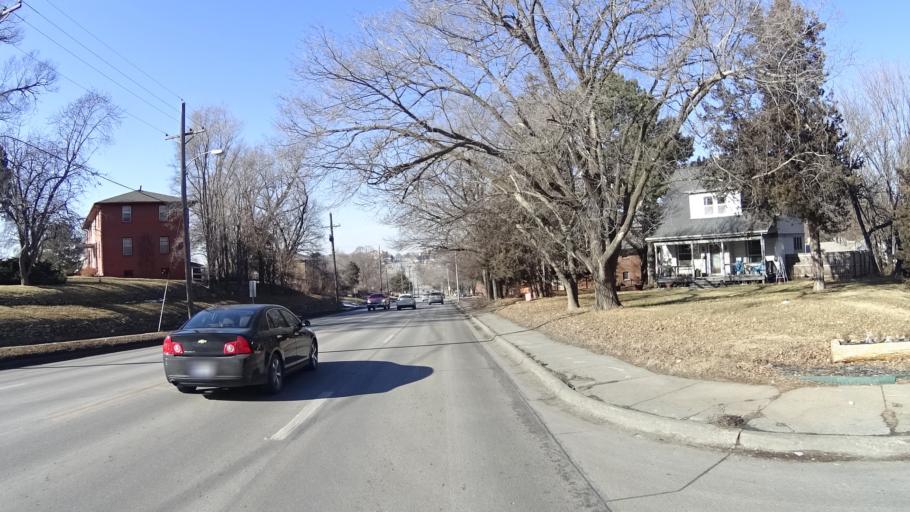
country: US
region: Nebraska
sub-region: Douglas County
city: Omaha
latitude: 41.2924
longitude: -96.0144
